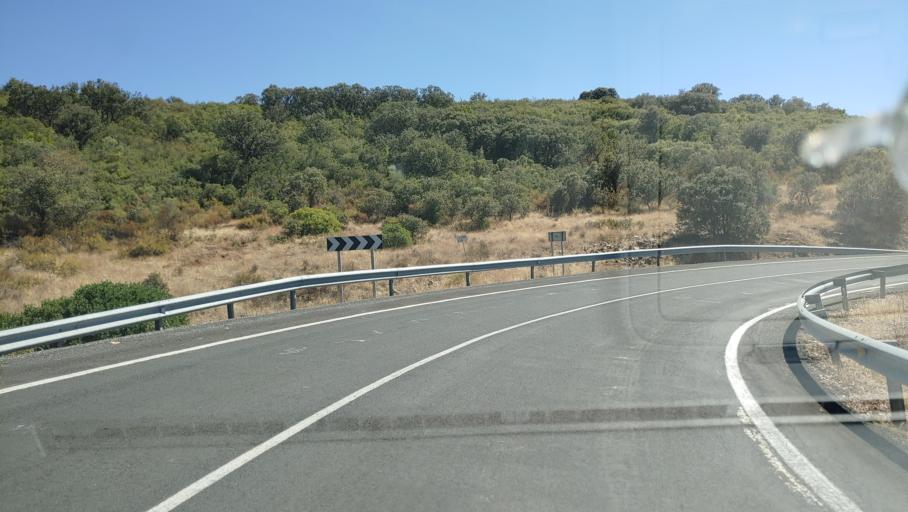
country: ES
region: Castille-La Mancha
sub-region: Provincia de Ciudad Real
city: Albaladejo
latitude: 38.5199
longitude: -2.7850
